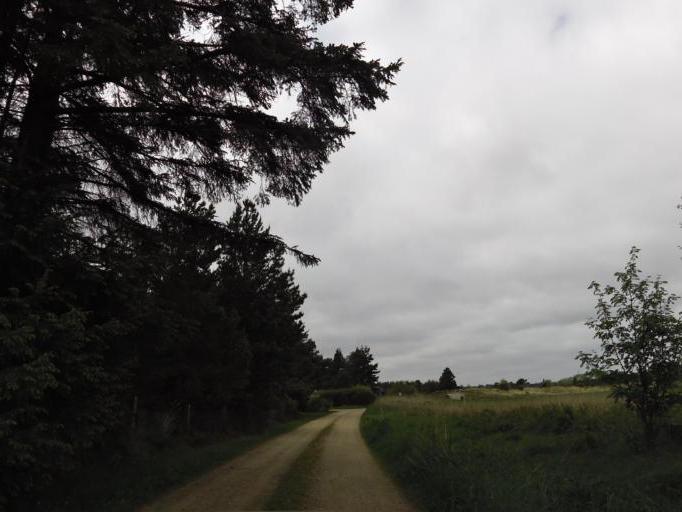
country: DE
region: Schleswig-Holstein
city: List
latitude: 55.1150
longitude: 8.5539
